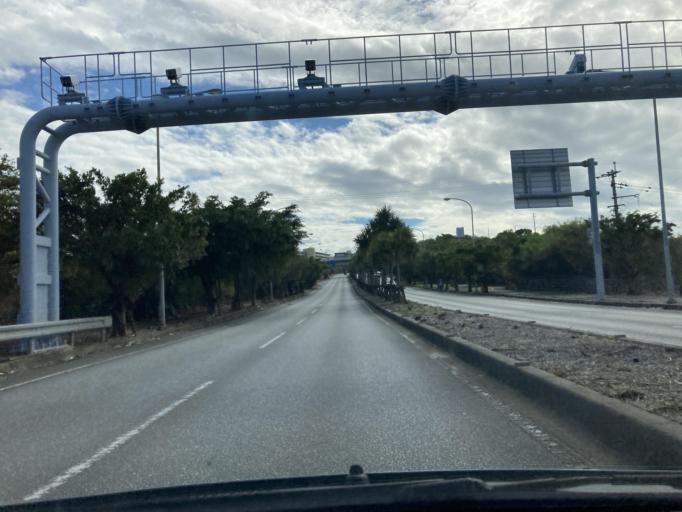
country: JP
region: Okinawa
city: Tomigusuku
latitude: 26.1682
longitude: 127.7260
